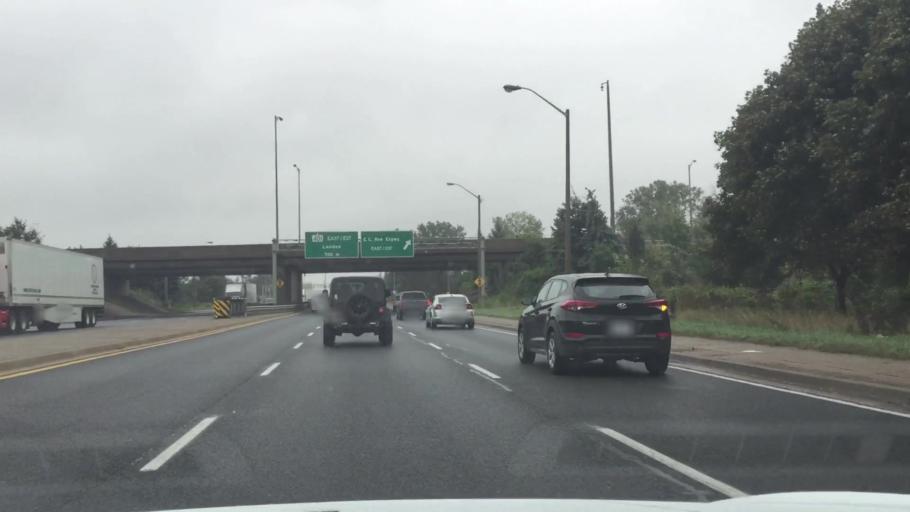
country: CA
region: Ontario
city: Windsor
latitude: 42.2718
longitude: -83.0484
